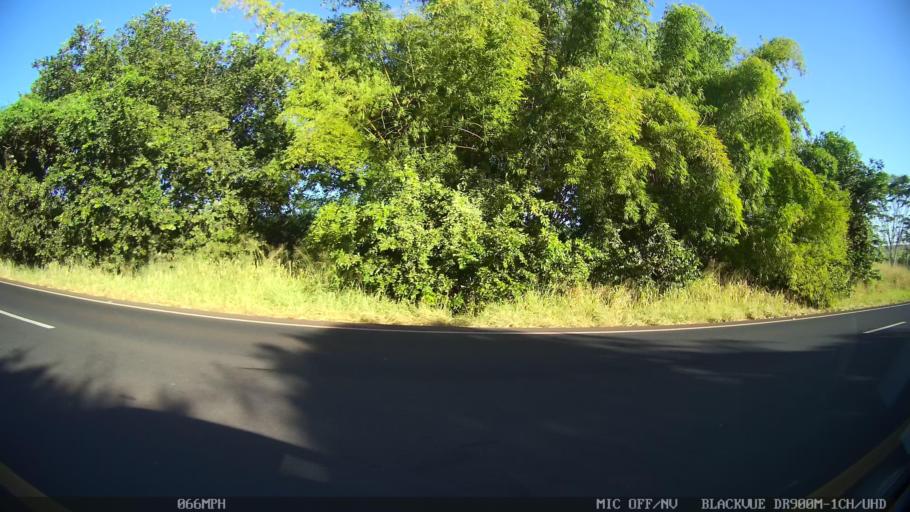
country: BR
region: Sao Paulo
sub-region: Olimpia
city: Olimpia
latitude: -20.7283
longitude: -49.0461
